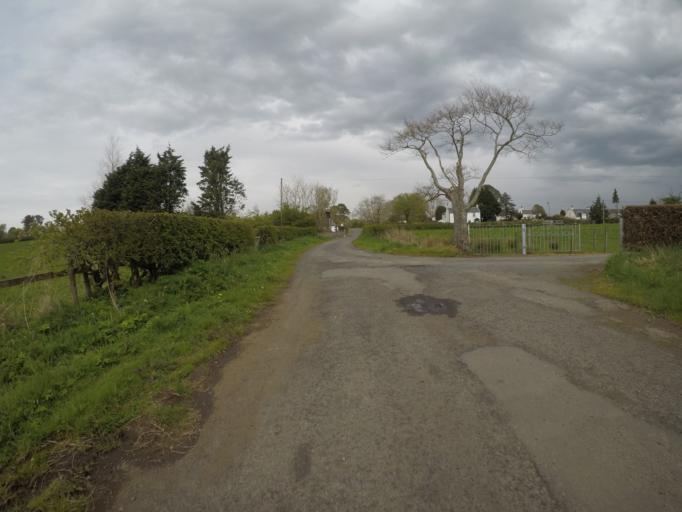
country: GB
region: Scotland
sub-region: East Ayrshire
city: Kilmarnock
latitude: 55.6565
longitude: -4.4472
